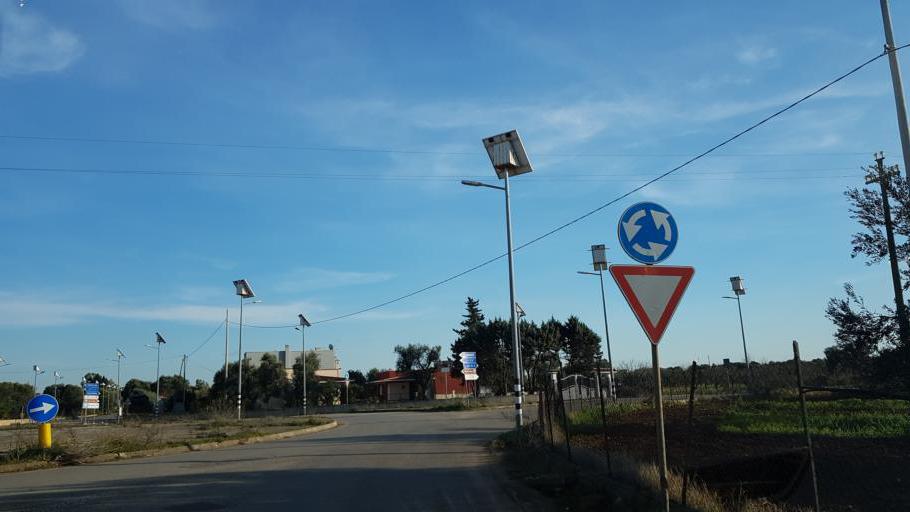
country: IT
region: Apulia
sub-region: Provincia di Brindisi
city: San Vito dei Normanni
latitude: 40.6949
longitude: 17.7583
